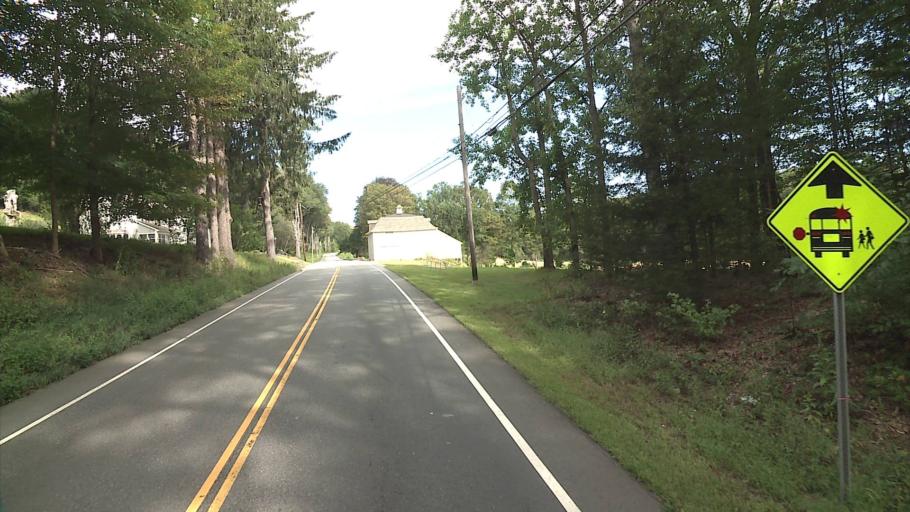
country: US
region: Connecticut
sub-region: New London County
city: Baltic
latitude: 41.6006
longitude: -72.1325
